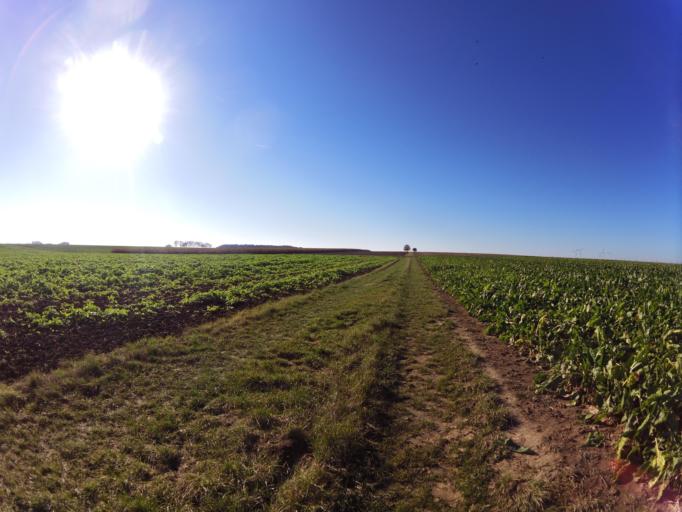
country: DE
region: Bavaria
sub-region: Regierungsbezirk Unterfranken
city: Giebelstadt
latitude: 49.6813
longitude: 9.9348
